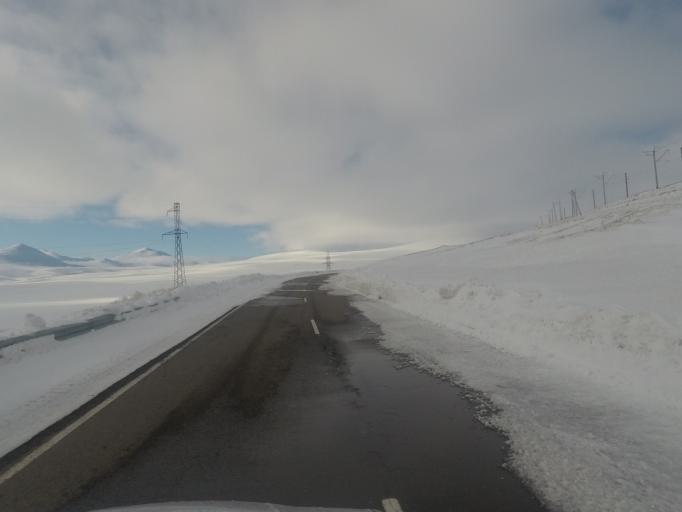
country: GE
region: Kvemo Kartli
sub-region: Tsalka
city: Tsalka
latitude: 41.4753
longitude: 43.8512
